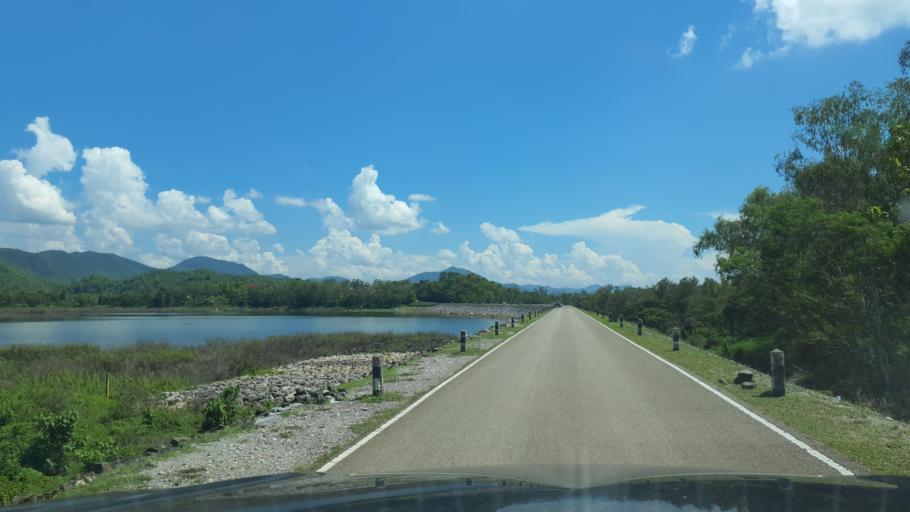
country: TH
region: Chiang Mai
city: Mae On
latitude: 18.8124
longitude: 99.2658
